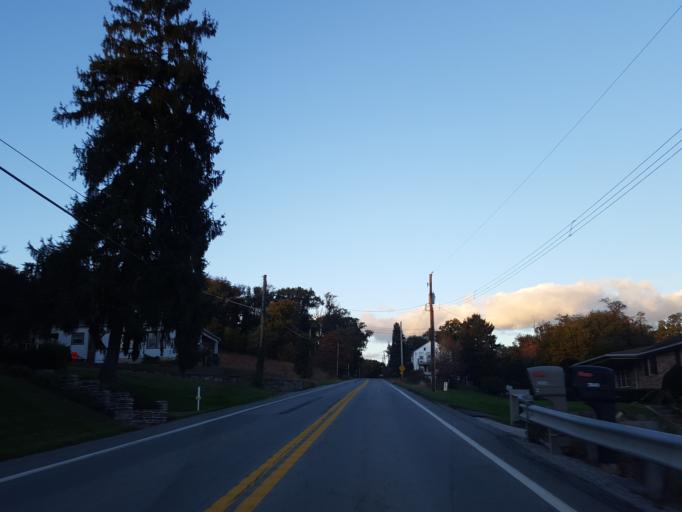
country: US
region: Pennsylvania
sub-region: York County
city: Wrightsville
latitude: 39.9491
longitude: -76.5081
